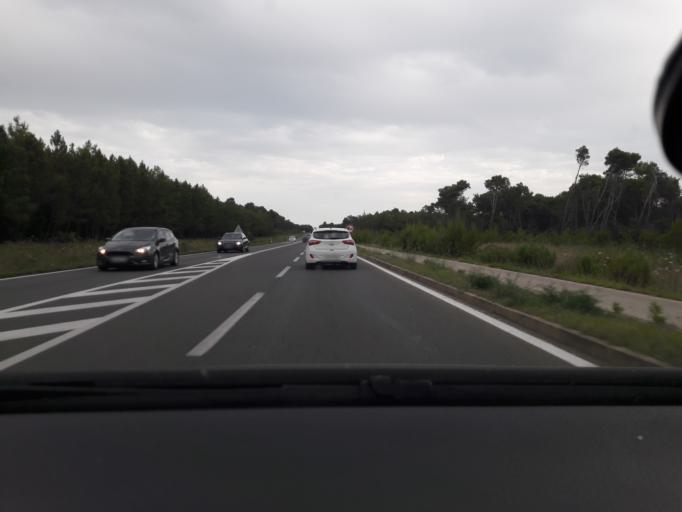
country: HR
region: Zadarska
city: Nin
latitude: 44.2093
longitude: 15.1776
